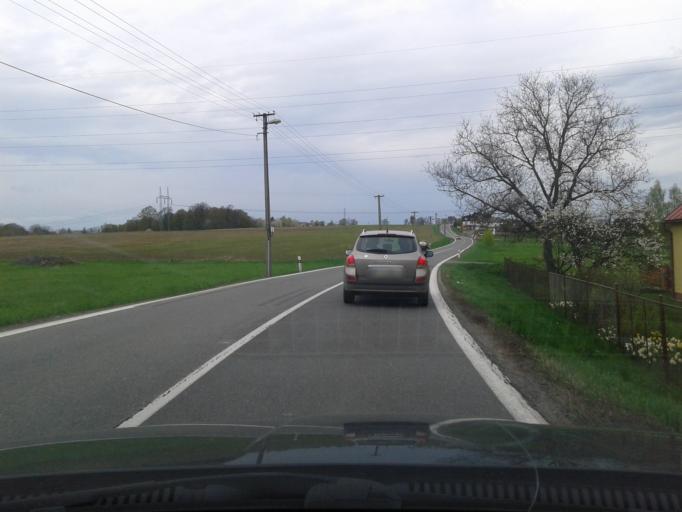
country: CZ
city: Sedliste
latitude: 49.7059
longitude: 18.3691
